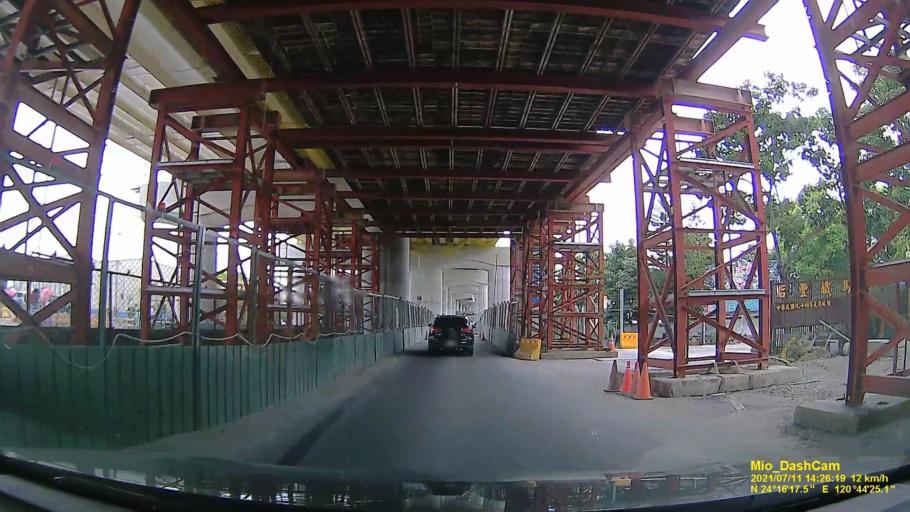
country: TW
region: Taiwan
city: Fengyuan
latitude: 24.2716
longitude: 120.7403
